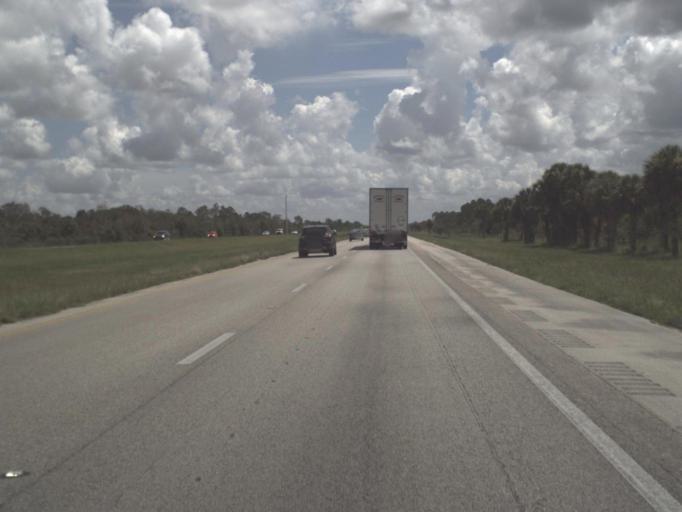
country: US
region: Florida
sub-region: Collier County
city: Orangetree
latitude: 26.1528
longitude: -81.5360
